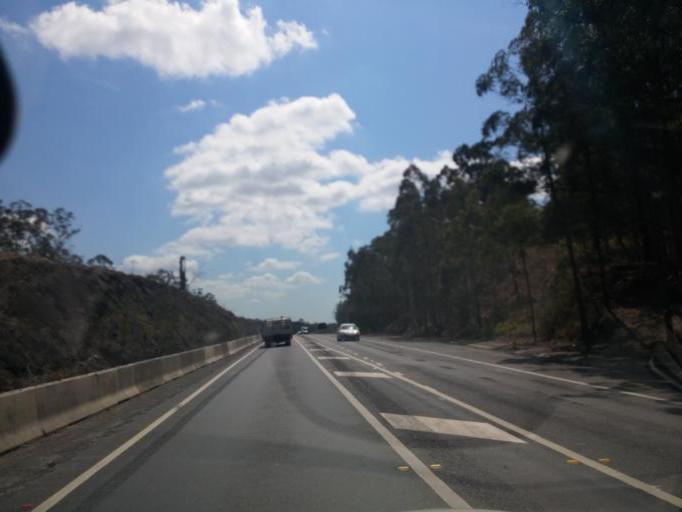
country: AU
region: New South Wales
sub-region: Port Macquarie-Hastings
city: North Shore
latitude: -31.2667
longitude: 152.8132
